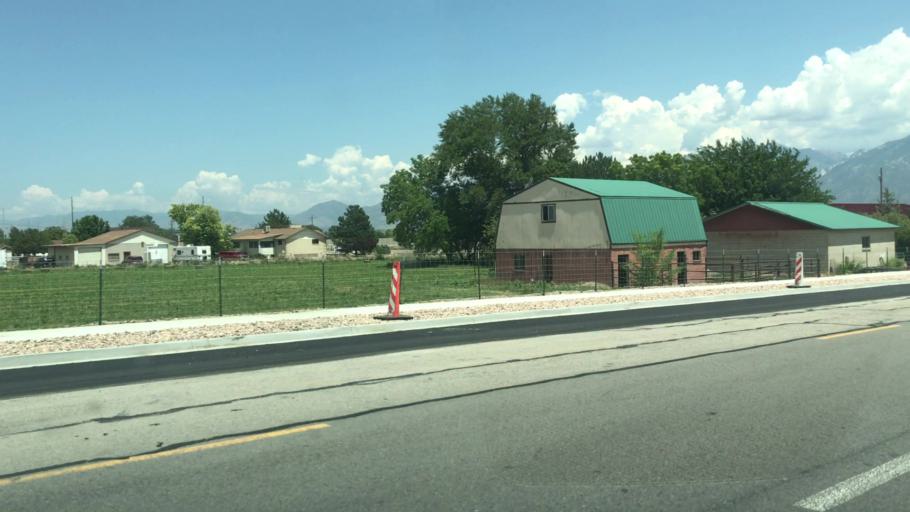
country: US
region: Utah
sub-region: Salt Lake County
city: Bluffdale
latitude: 40.4967
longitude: -111.9596
